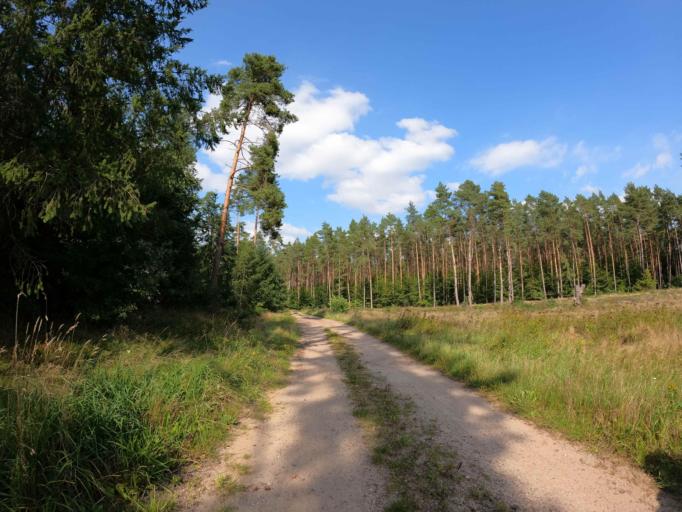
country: DE
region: Mecklenburg-Vorpommern
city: Malchow
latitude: 53.5271
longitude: 12.4706
